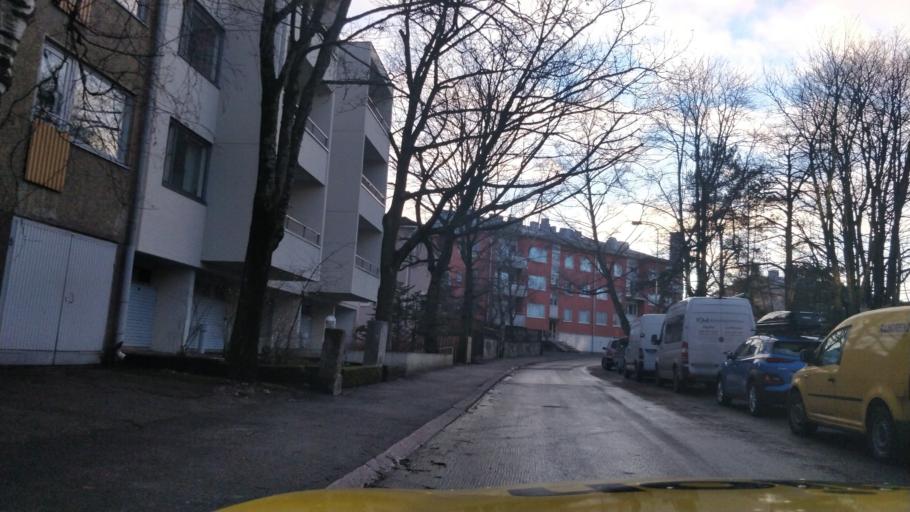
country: FI
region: Uusimaa
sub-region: Helsinki
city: Helsinki
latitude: 60.2108
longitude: 24.8955
